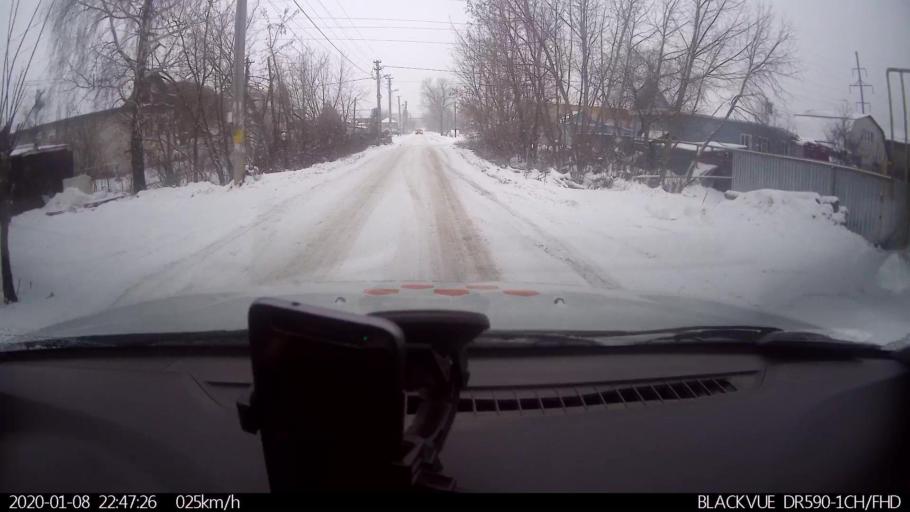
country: RU
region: Nizjnij Novgorod
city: Nizhniy Novgorod
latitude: 56.2923
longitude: 43.8934
